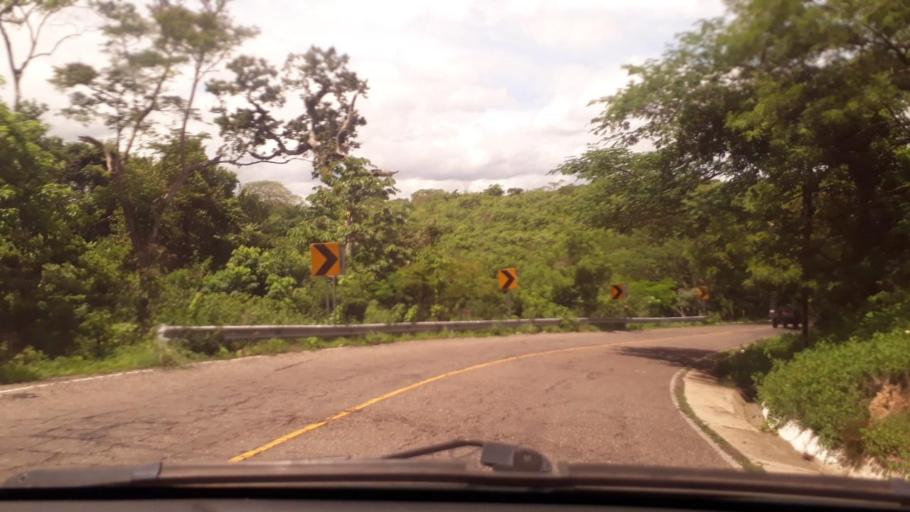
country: GT
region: Jutiapa
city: Jalpatagua
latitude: 14.1646
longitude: -90.0501
